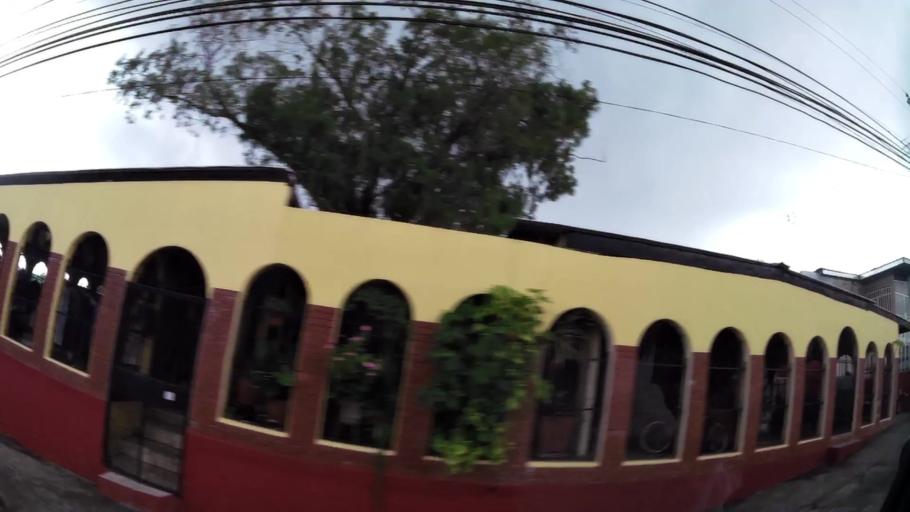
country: PA
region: Panama
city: San Miguelito
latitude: 9.0545
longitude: -79.4440
